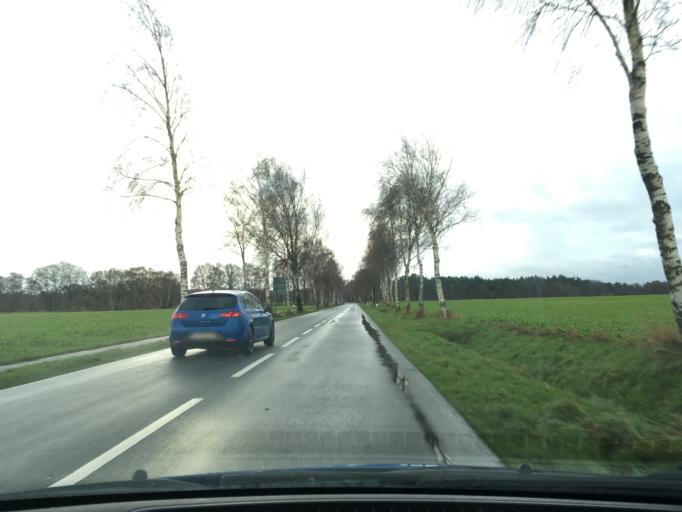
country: DE
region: Lower Saxony
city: Embsen
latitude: 53.1855
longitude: 10.3312
